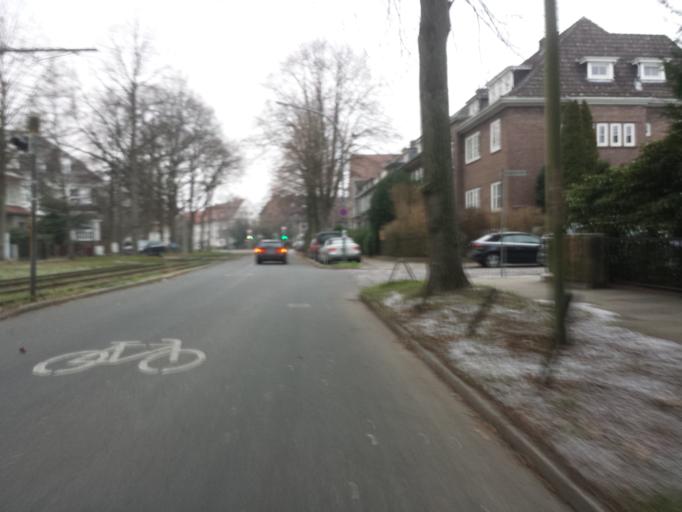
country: DE
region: Bremen
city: Bremen
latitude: 53.0881
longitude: 8.8406
